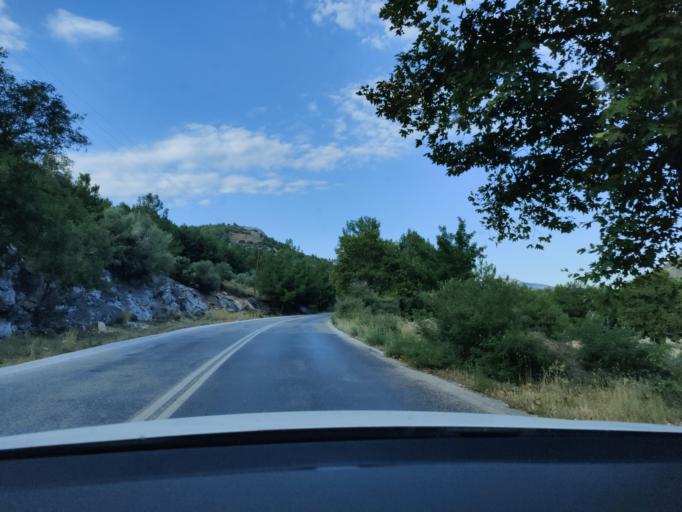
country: GR
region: East Macedonia and Thrace
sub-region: Nomos Kavalas
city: Limenaria
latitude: 40.6149
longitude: 24.6371
